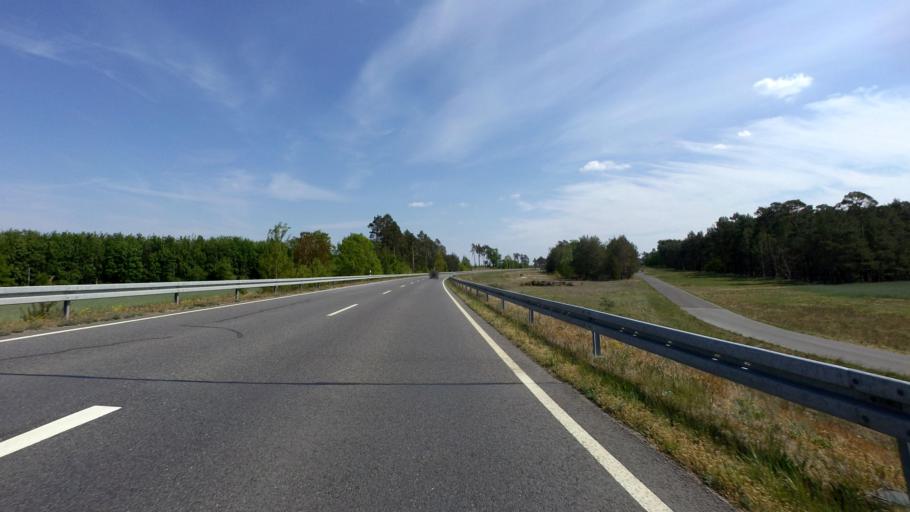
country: DE
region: Brandenburg
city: Cottbus
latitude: 51.7838
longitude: 14.3820
